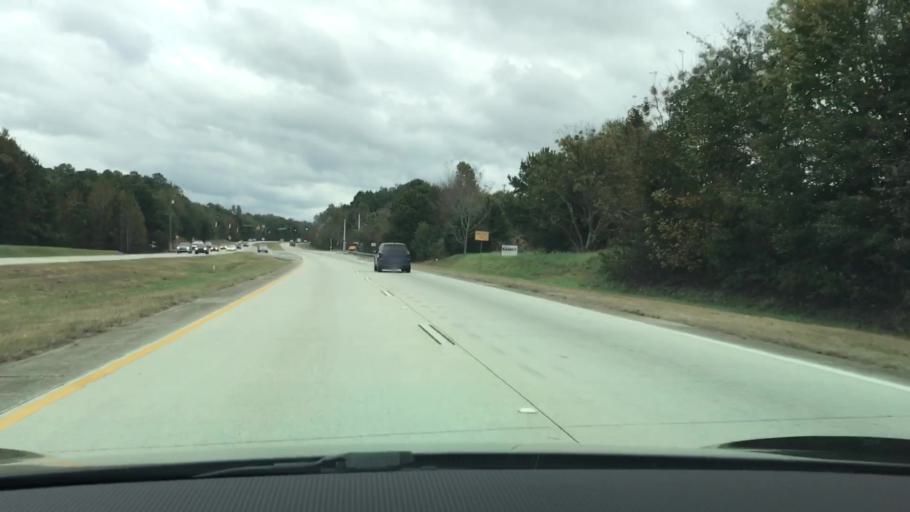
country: US
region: Georgia
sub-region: Oconee County
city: Bogart
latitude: 33.9174
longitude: -83.4846
